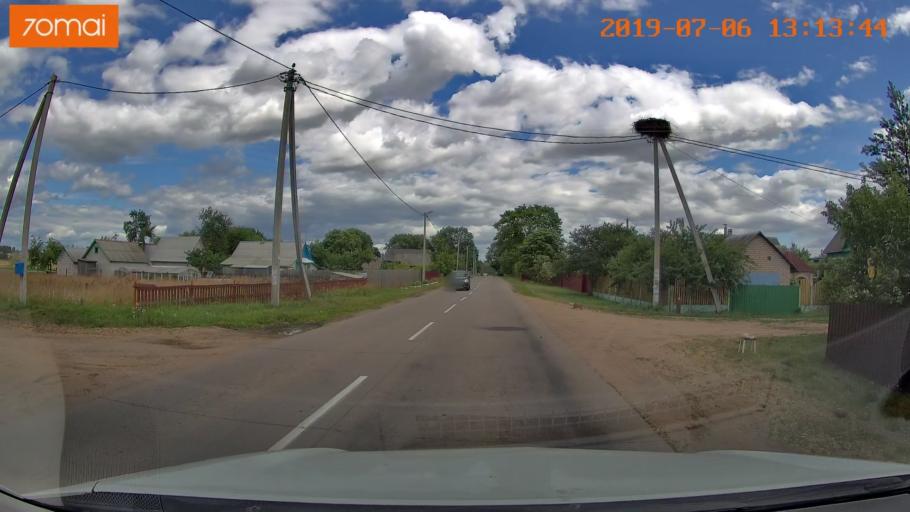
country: BY
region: Minsk
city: Enyerhyetykaw
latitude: 53.6593
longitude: 27.0051
